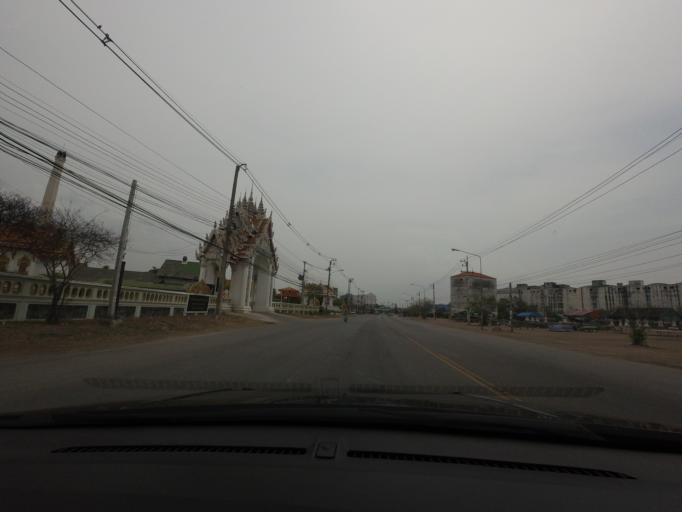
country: TH
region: Phetchaburi
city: Ban Laem
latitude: 13.2107
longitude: 99.9772
